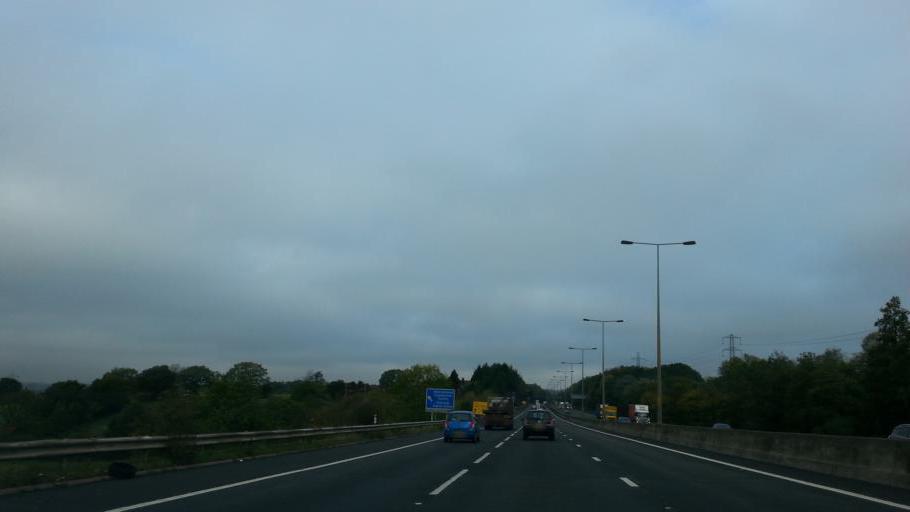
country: GB
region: England
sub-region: City and Borough of Birmingham
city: Bartley Green
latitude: 52.4360
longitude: -2.0177
